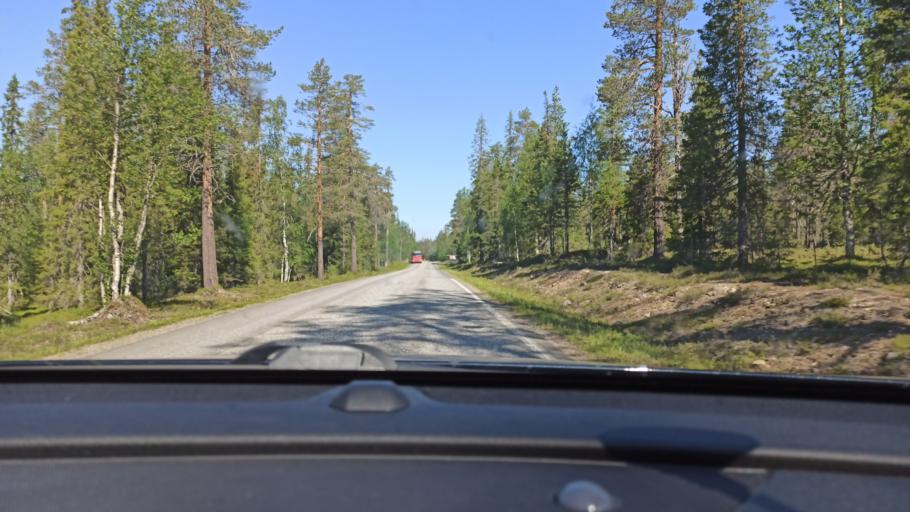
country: FI
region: Lapland
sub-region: Tunturi-Lappi
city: Kolari
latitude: 67.6638
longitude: 24.1627
